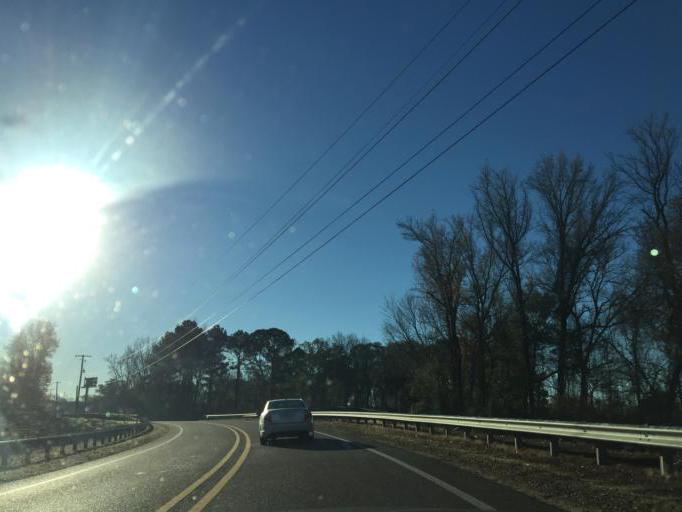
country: US
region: Mississippi
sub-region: Hinds County
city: Jackson
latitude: 32.2857
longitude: -90.1743
